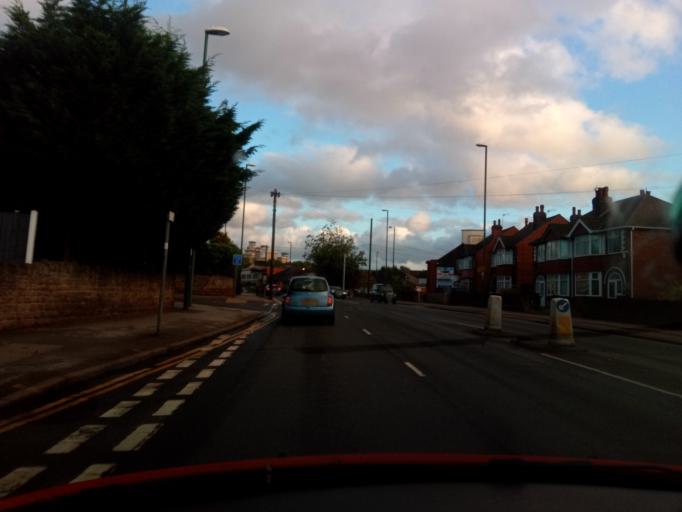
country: GB
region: England
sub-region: Nottingham
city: Nottingham
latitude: 52.9653
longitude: -1.1812
